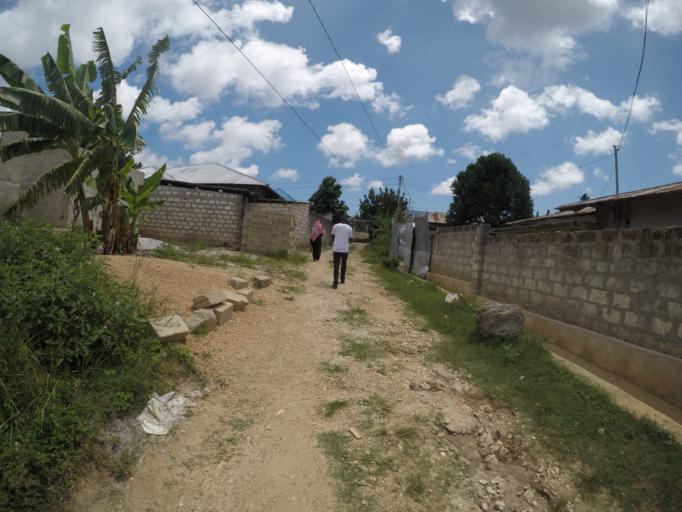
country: TZ
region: Pemba South
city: Chake Chake
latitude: -5.2312
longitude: 39.7795
